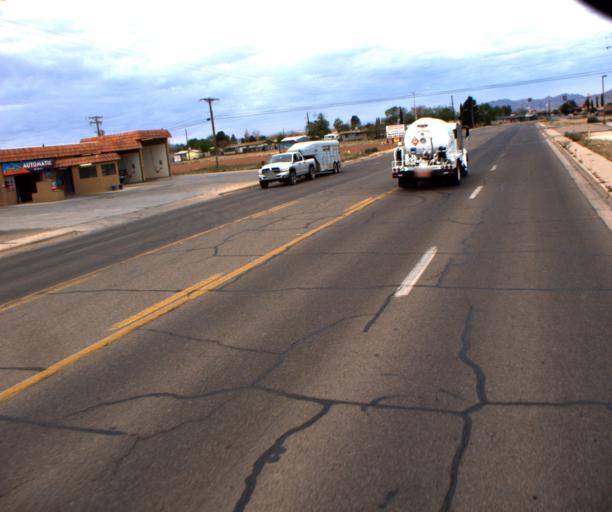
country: US
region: Arizona
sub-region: Cochise County
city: Willcox
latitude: 32.2641
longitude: -109.8325
